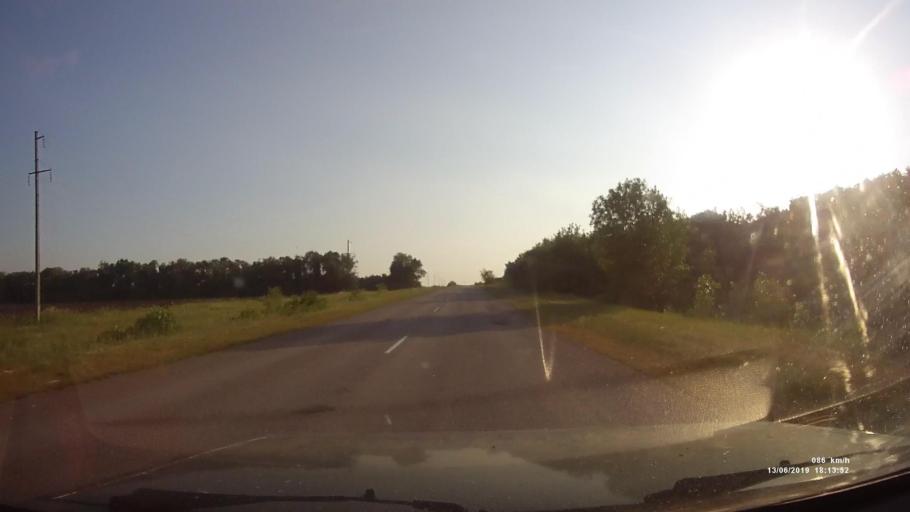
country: RU
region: Rostov
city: Kazanskaya
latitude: 49.9366
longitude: 41.3868
